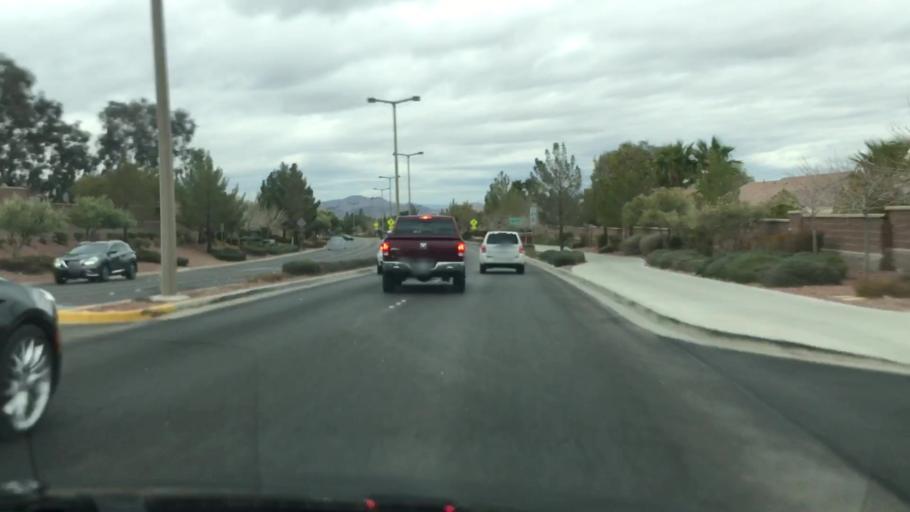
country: US
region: Nevada
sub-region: Clark County
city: Whitney
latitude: 35.9473
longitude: -115.0959
